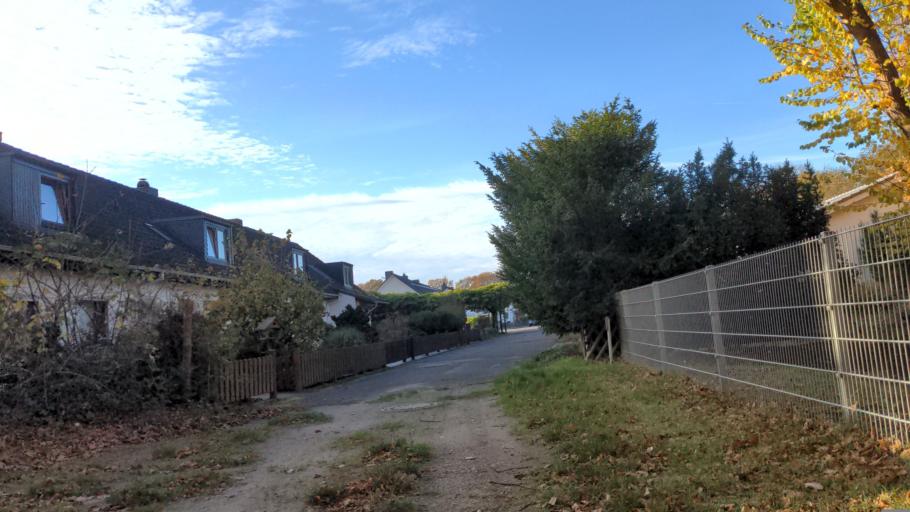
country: DE
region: Schleswig-Holstein
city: Gross Gronau
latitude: 53.8394
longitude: 10.7479
